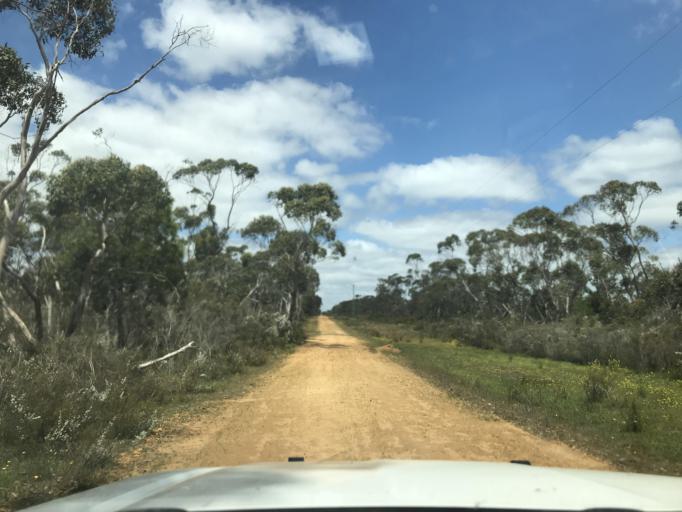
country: AU
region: South Australia
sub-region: Wattle Range
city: Penola
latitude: -37.3686
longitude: 141.1600
